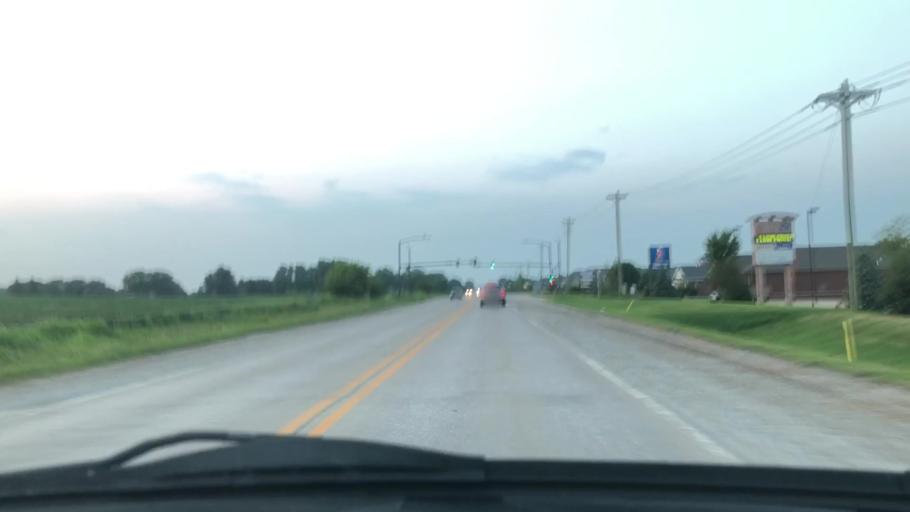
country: US
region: Iowa
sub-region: Johnson County
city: North Liberty
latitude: 41.7272
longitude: -91.6077
